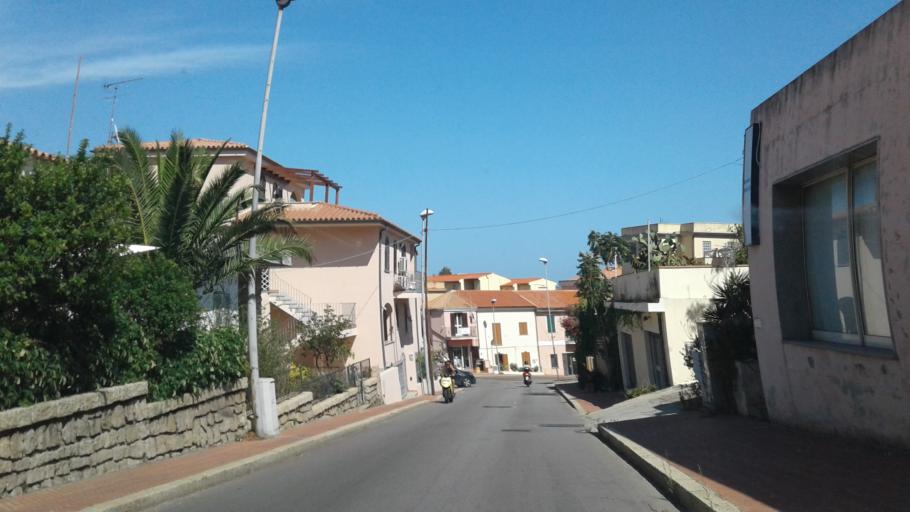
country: IT
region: Sardinia
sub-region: Provincia di Olbia-Tempio
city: La Maddalena
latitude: 41.2169
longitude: 9.4081
